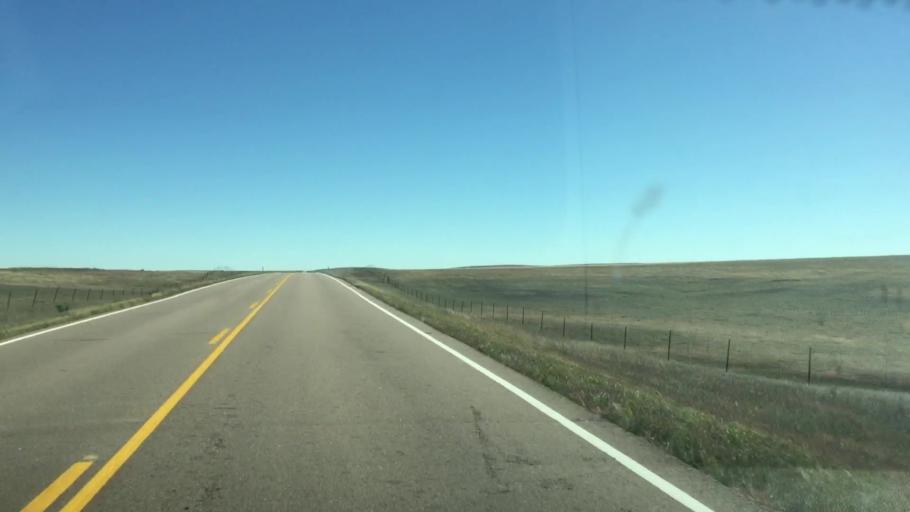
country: US
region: Colorado
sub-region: Lincoln County
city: Limon
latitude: 39.2761
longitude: -104.0025
